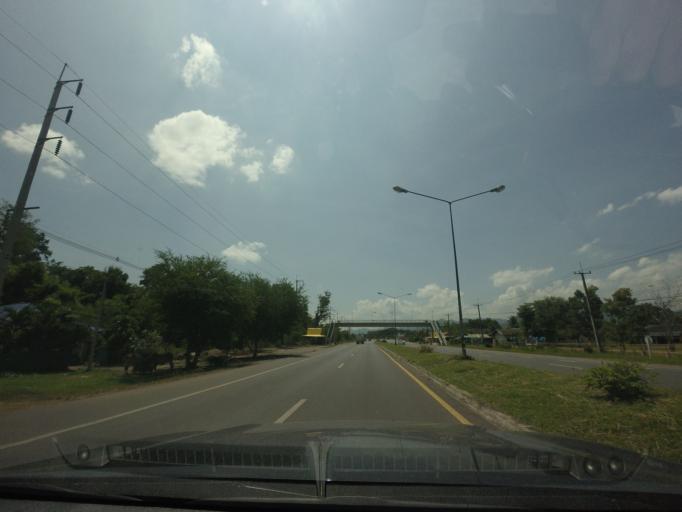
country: TH
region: Phetchabun
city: Lom Sak
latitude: 16.6900
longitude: 101.1667
